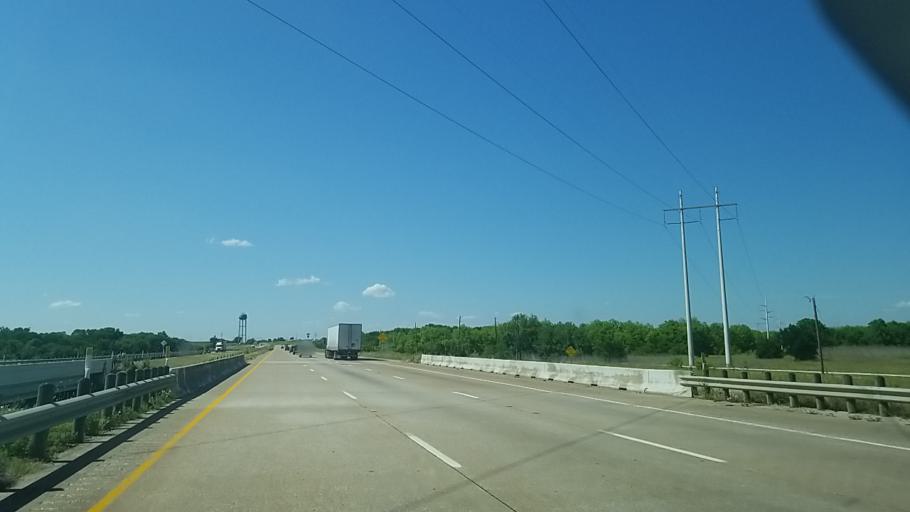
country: US
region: Texas
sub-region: Ellis County
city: Palmer
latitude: 32.4048
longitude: -96.6568
